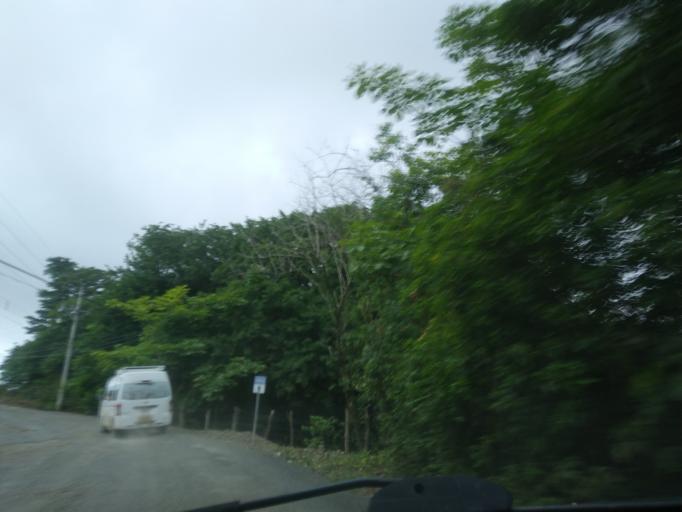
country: CR
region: Puntarenas
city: Paquera
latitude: 9.6506
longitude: -85.1356
